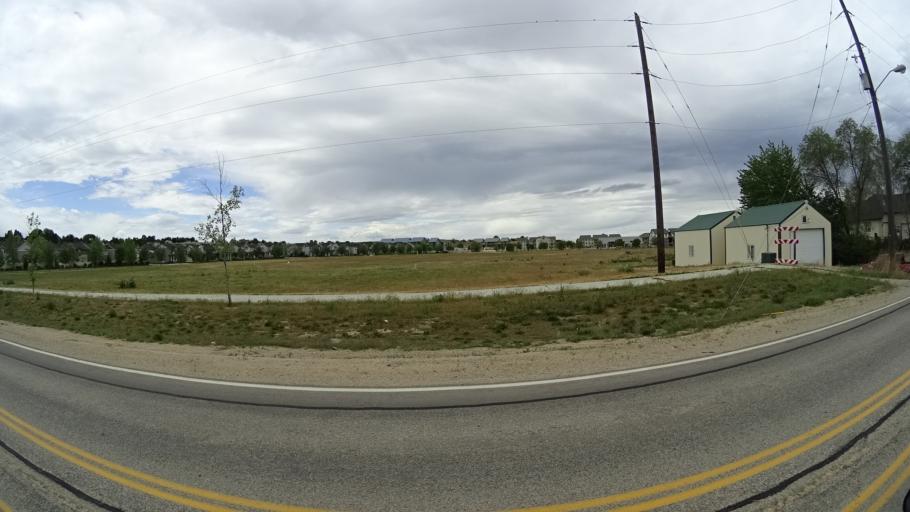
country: US
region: Idaho
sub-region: Ada County
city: Meridian
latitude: 43.5874
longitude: -116.4137
